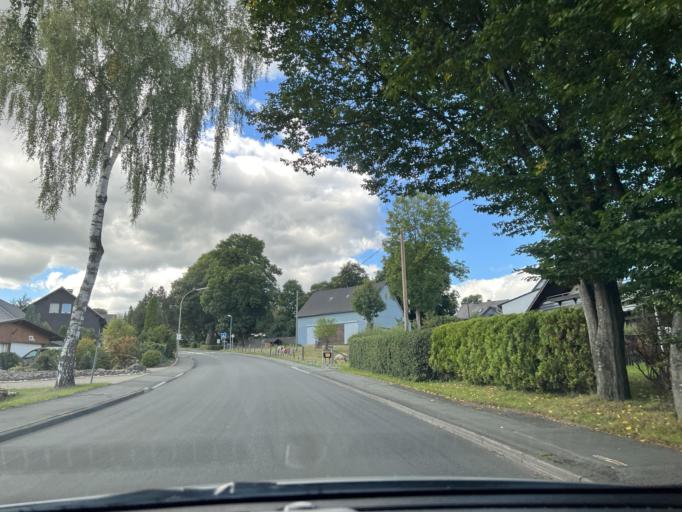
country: DE
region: North Rhine-Westphalia
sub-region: Regierungsbezirk Arnsberg
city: Bad Berleburg
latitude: 51.0132
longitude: 8.3641
